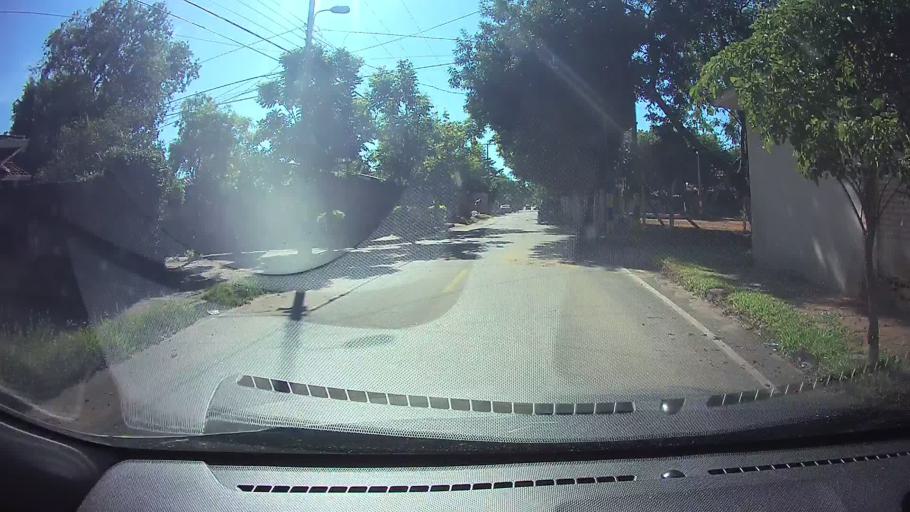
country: PY
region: Central
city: Fernando de la Mora
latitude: -25.2770
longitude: -57.5134
